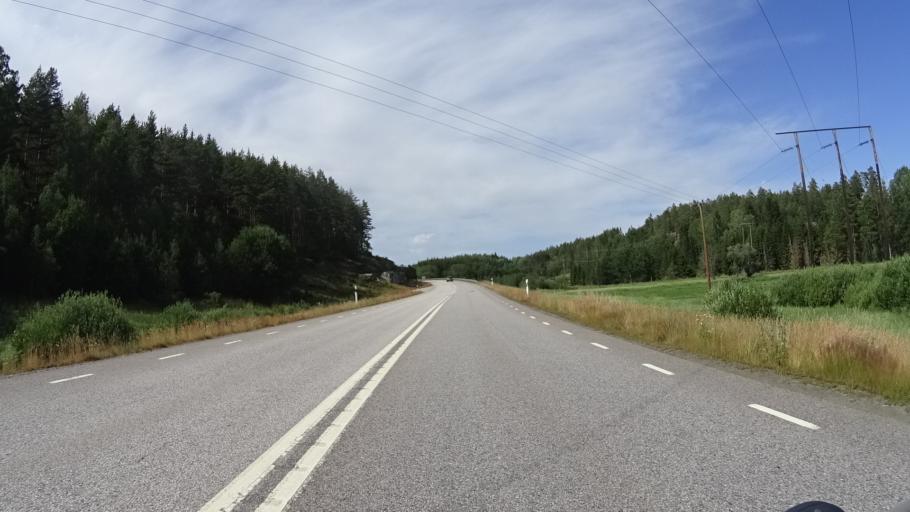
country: SE
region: Kalmar
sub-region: Vasterviks Kommun
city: Overum
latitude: 57.9700
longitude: 16.3375
